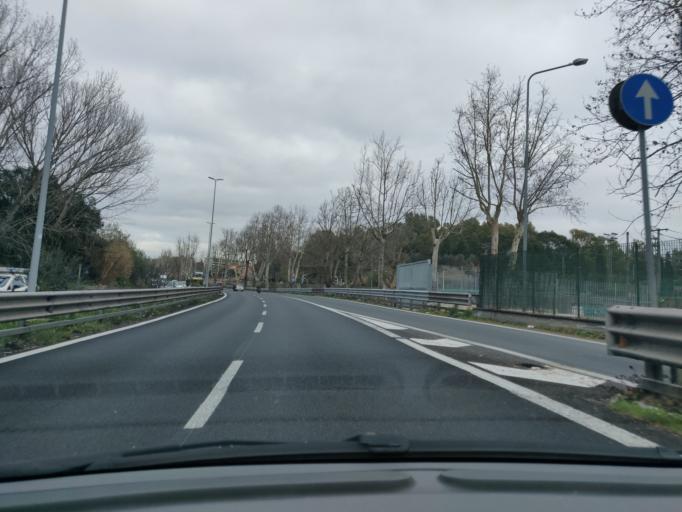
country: IT
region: Latium
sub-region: Citta metropolitana di Roma Capitale
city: La Massimina-Casal Lumbroso
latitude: 41.8841
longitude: 12.3956
